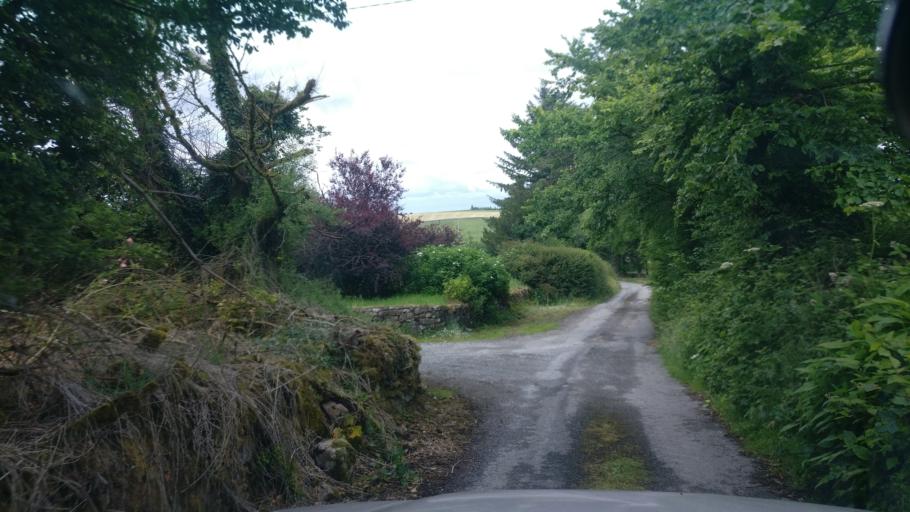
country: IE
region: Connaught
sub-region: County Galway
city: Loughrea
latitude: 53.1518
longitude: -8.5570
